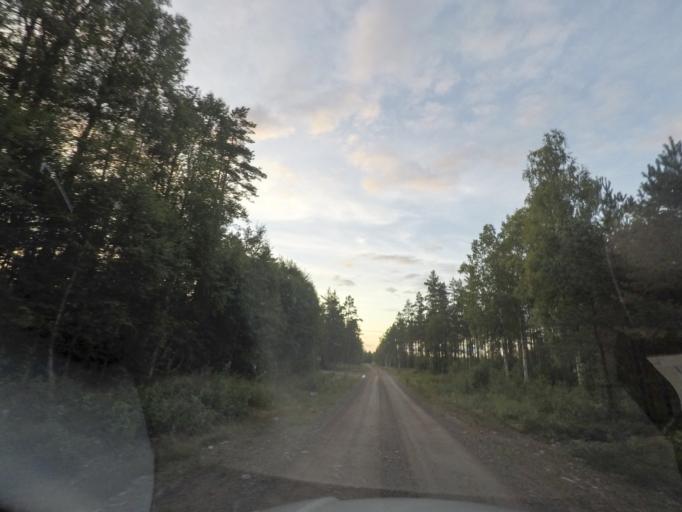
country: SE
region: OErebro
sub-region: Hallefors Kommun
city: Haellefors
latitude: 59.9683
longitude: 14.5340
